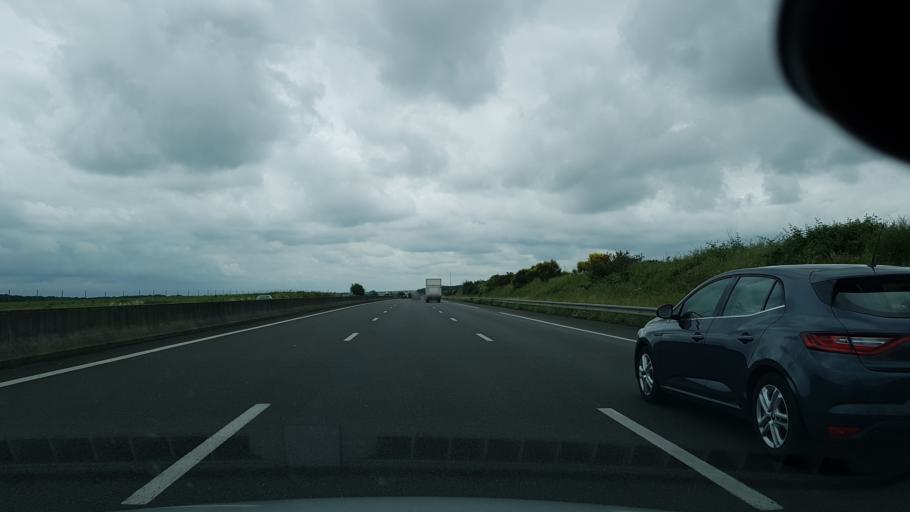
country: FR
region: Centre
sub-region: Departement d'Indre-et-Loire
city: Cangey
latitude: 47.5668
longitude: 1.0434
